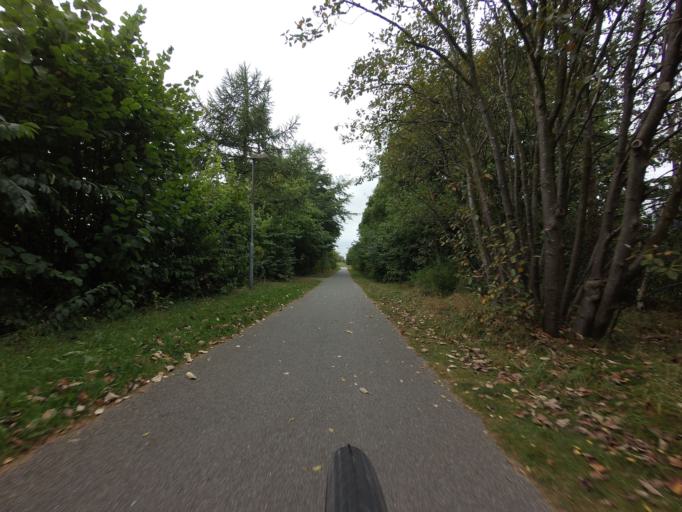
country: DK
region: South Denmark
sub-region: Billund Kommune
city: Grindsted
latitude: 55.7652
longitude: 8.9184
